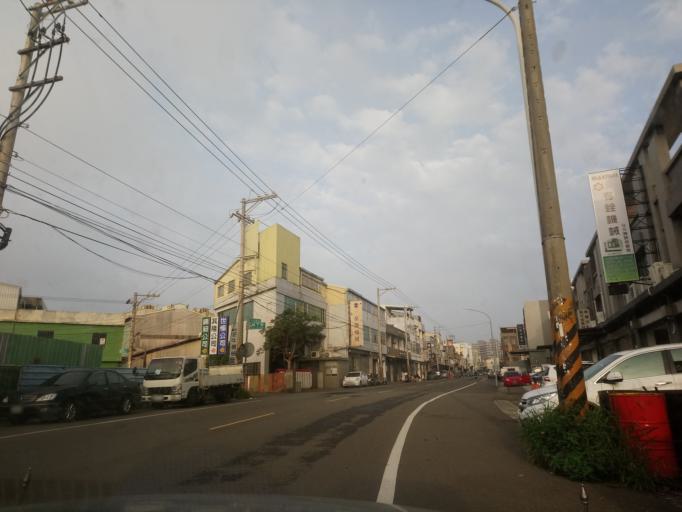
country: TW
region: Taiwan
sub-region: Hsinchu
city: Hsinchu
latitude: 24.7951
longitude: 120.9329
